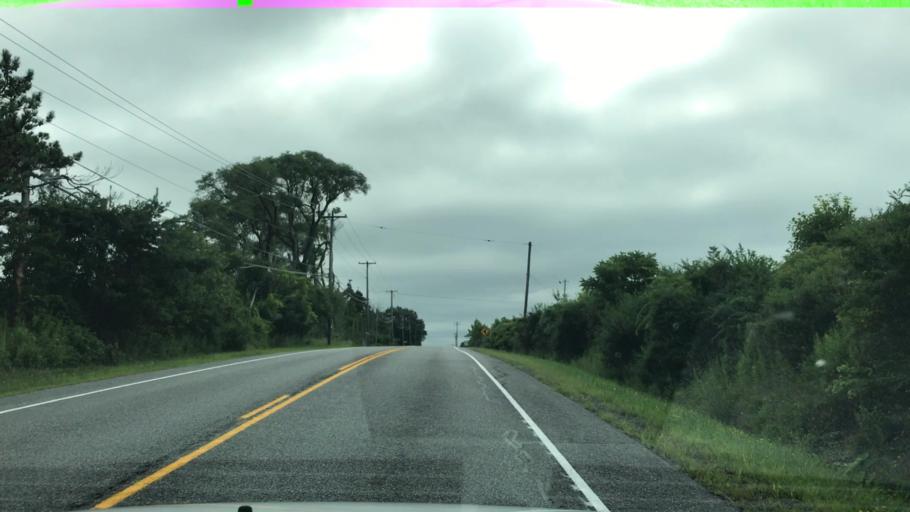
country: US
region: New York
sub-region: Wyoming County
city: Attica
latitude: 42.8360
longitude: -78.3684
